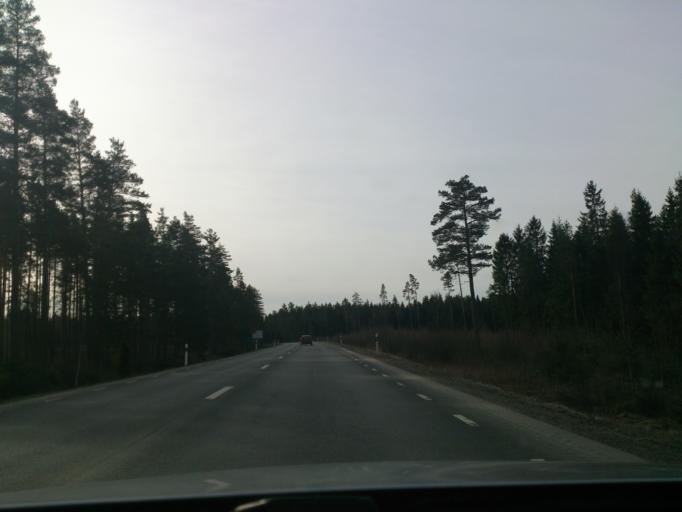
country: SE
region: Kronoberg
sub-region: Alvesta Kommun
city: Moheda
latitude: 56.9980
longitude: 14.5593
